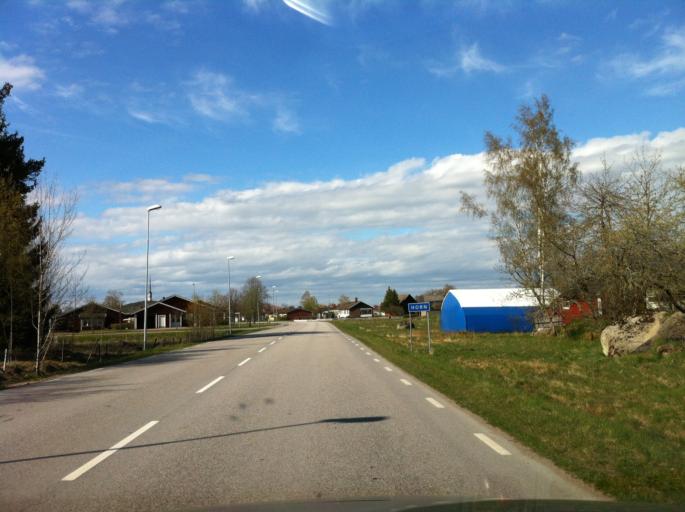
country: SE
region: Kalmar
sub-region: Vimmerby Kommun
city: Sodra Vi
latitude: 57.8638
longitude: 15.8382
